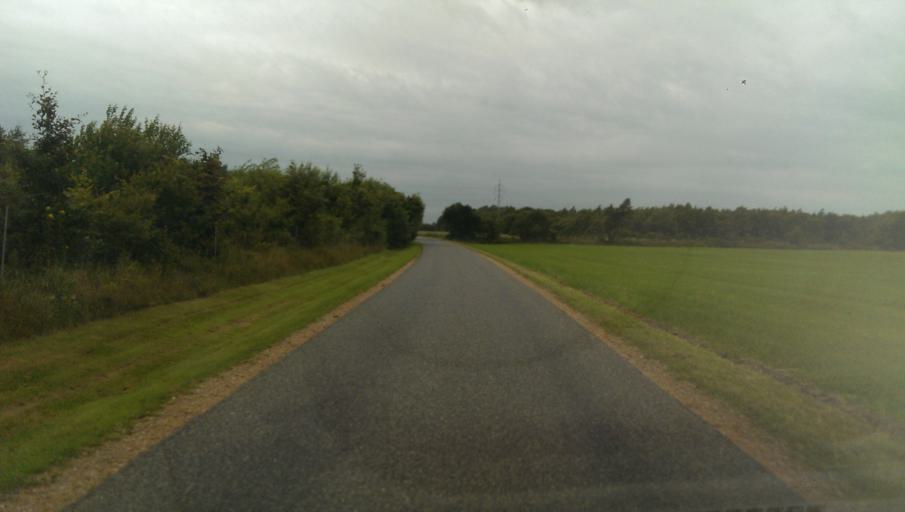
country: DK
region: South Denmark
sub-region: Esbjerg Kommune
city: Bramming
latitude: 55.4772
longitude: 8.7247
